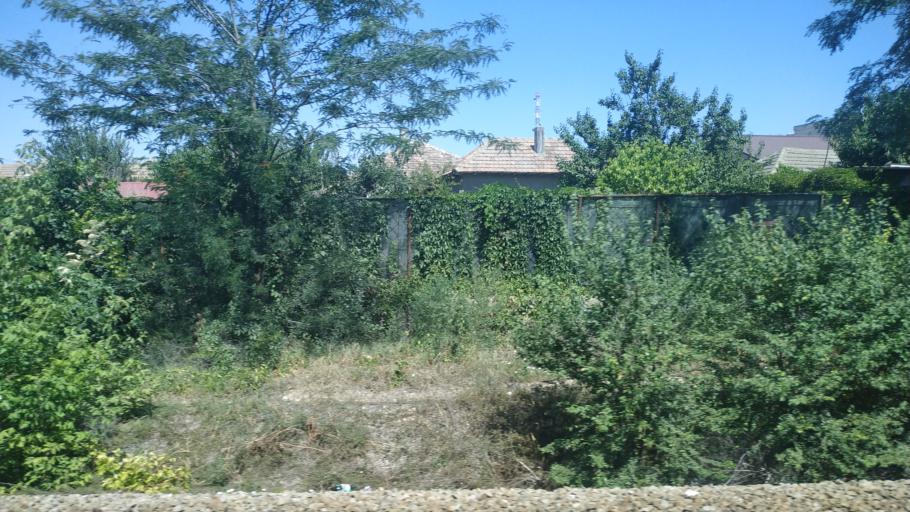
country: RO
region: Constanta
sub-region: Oras Murfatlar
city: Murfatlar
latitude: 44.1728
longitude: 28.4091
